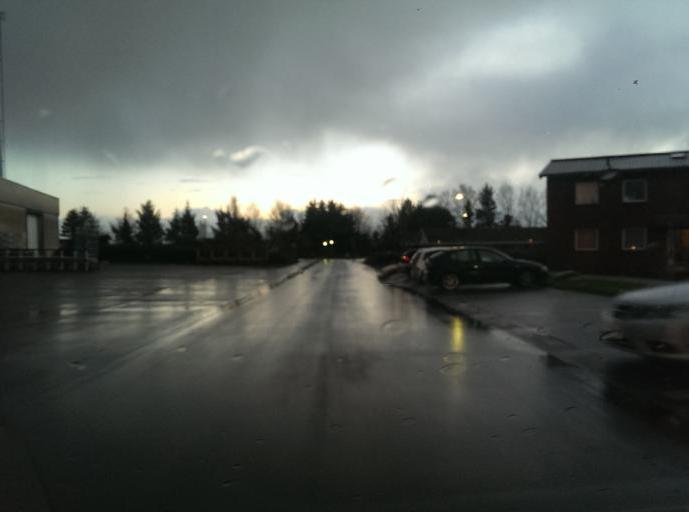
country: DK
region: South Denmark
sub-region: Esbjerg Kommune
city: Bramming
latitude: 55.4651
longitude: 8.6888
